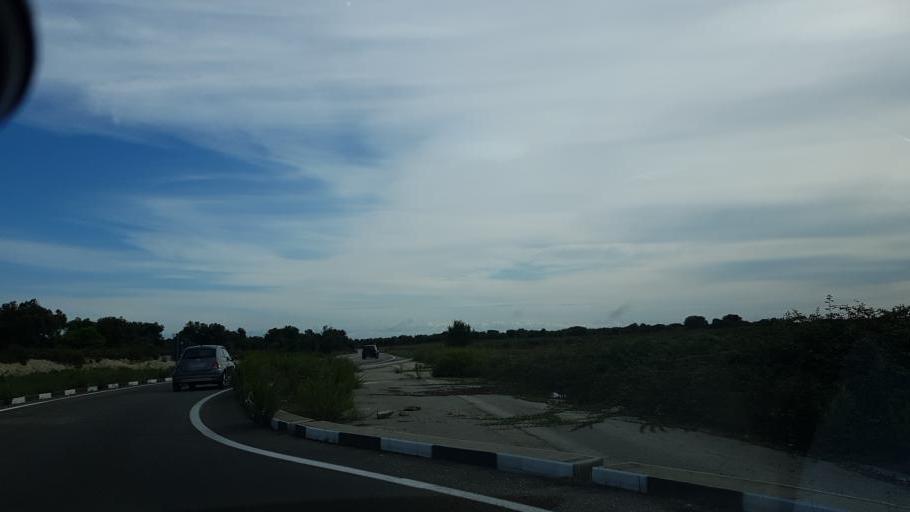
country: IT
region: Apulia
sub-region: Provincia di Lecce
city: Vernole
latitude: 40.3288
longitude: 18.3370
